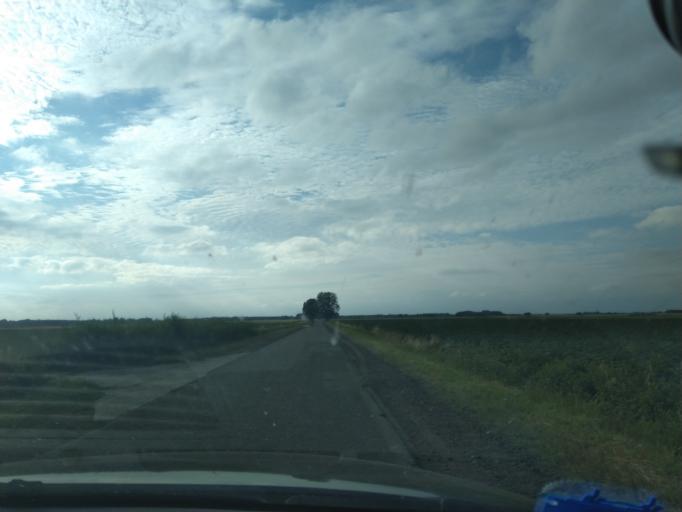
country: NL
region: Groningen
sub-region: Gemeente Vlagtwedde
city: Vlagtwedde
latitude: 53.0773
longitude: 7.1155
